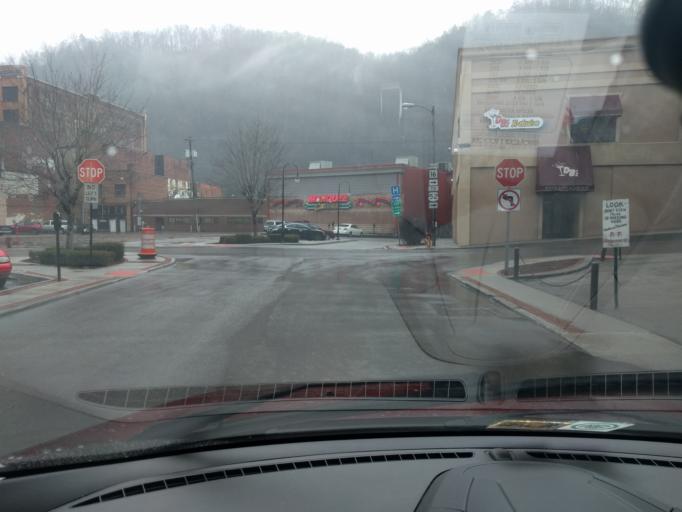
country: US
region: West Virginia
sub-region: McDowell County
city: Welch
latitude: 37.4319
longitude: -81.5843
